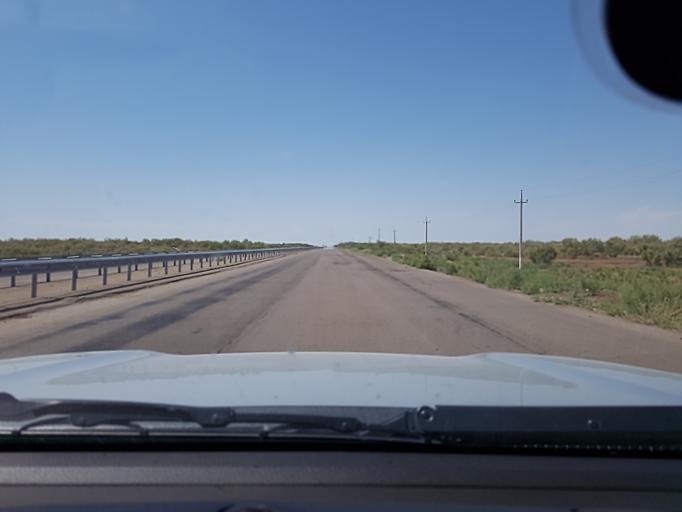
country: TM
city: Akdepe
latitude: 41.7367
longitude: 59.0272
